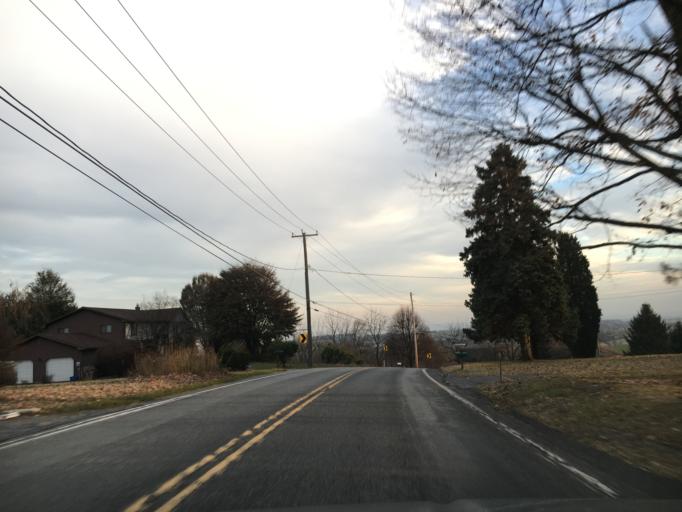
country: US
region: Pennsylvania
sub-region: Lehigh County
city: Slatington
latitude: 40.7153
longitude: -75.5966
